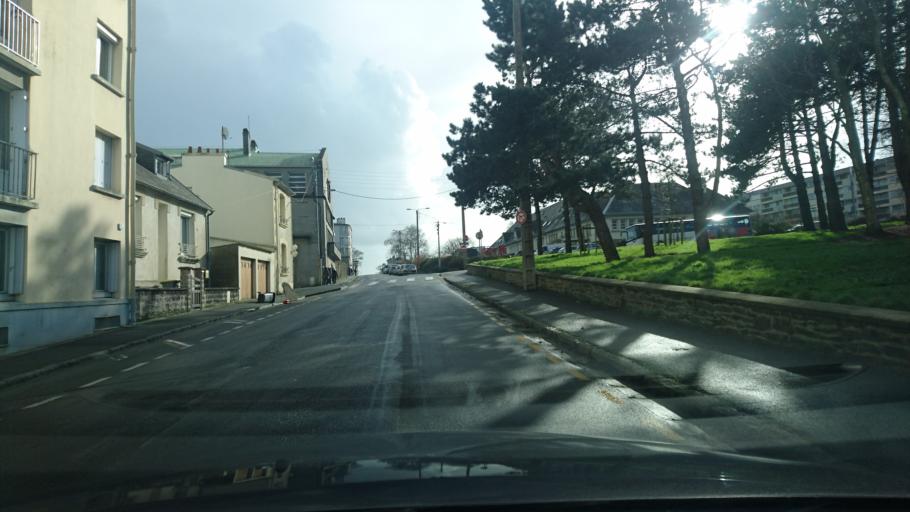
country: FR
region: Brittany
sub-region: Departement du Finistere
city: Brest
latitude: 48.3884
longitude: -4.5034
